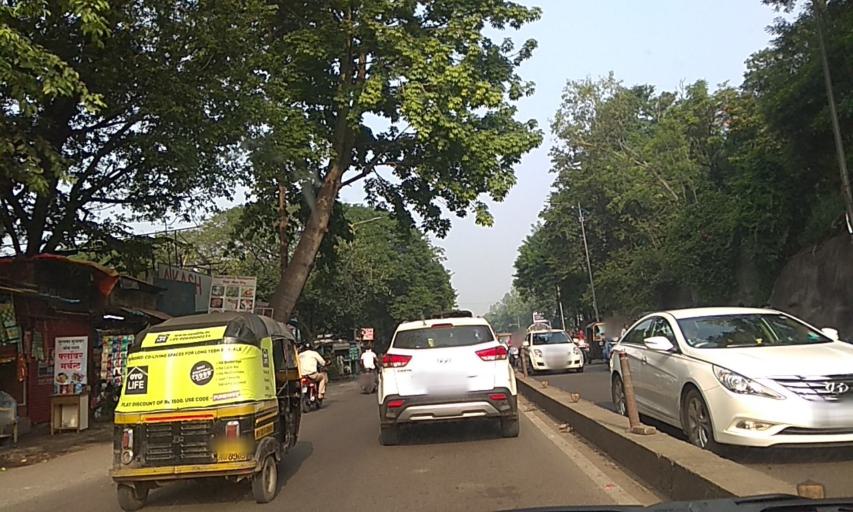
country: IN
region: Maharashtra
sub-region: Pune Division
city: Shivaji Nagar
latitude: 18.5439
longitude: 73.8785
